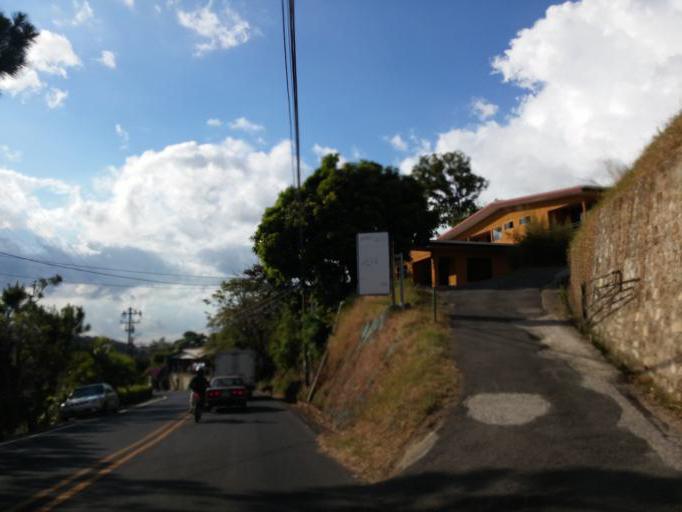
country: CR
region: San Jose
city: San Ignacio
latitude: 9.7956
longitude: -84.1500
